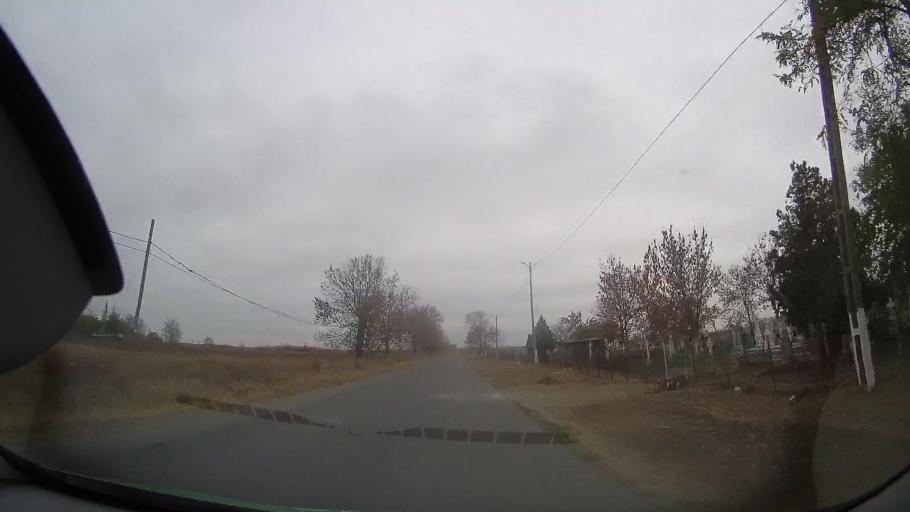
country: RO
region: Braila
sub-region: Comuna Ulmu
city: Ulmu
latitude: 44.9568
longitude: 27.3023
